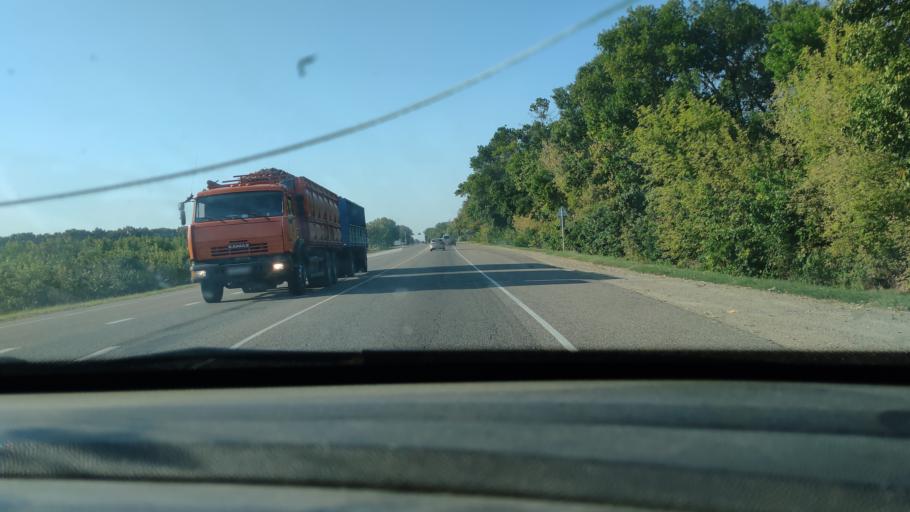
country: RU
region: Krasnodarskiy
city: Medvedovskaya
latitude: 45.4493
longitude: 38.9922
